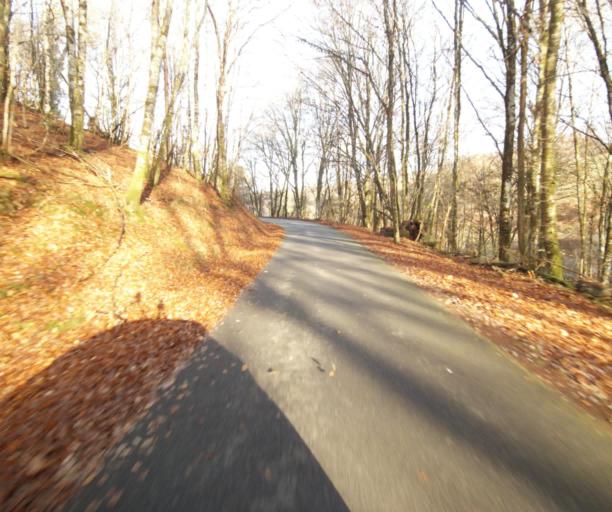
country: FR
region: Limousin
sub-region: Departement de la Correze
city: Laguenne
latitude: 45.2623
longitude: 1.8019
